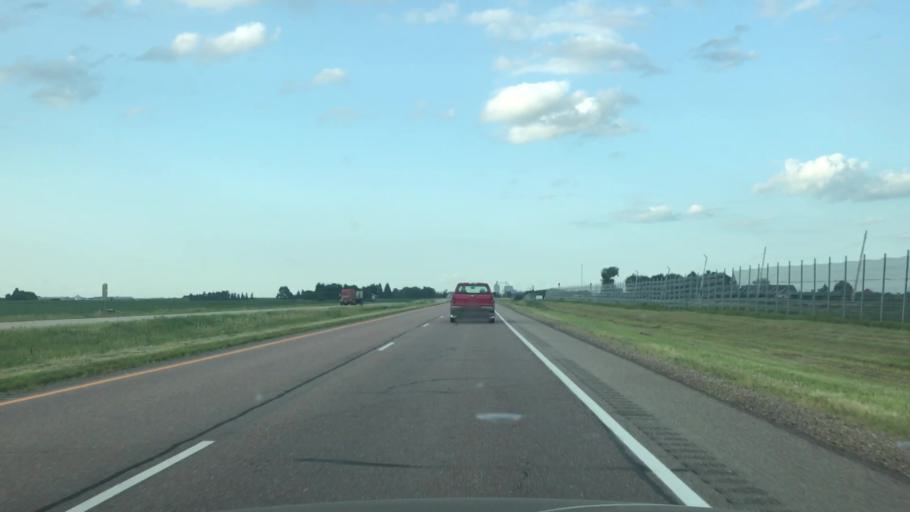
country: US
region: Minnesota
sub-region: Nobles County
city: Worthington
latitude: 43.6780
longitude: -95.5032
